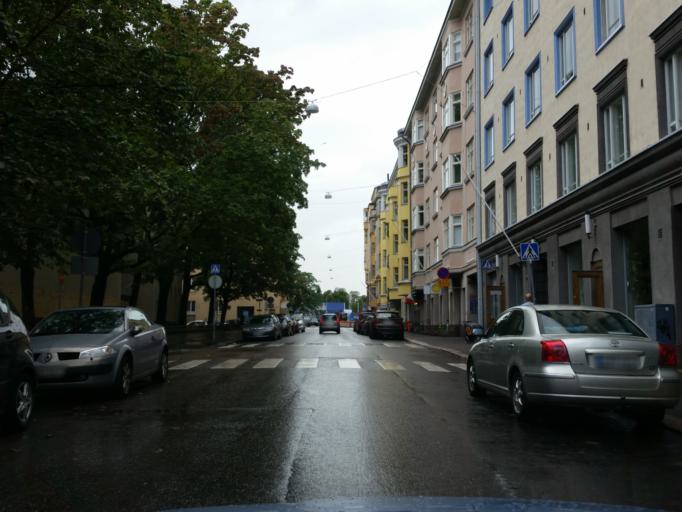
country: FI
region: Uusimaa
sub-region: Helsinki
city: Helsinki
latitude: 60.1671
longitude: 24.9262
